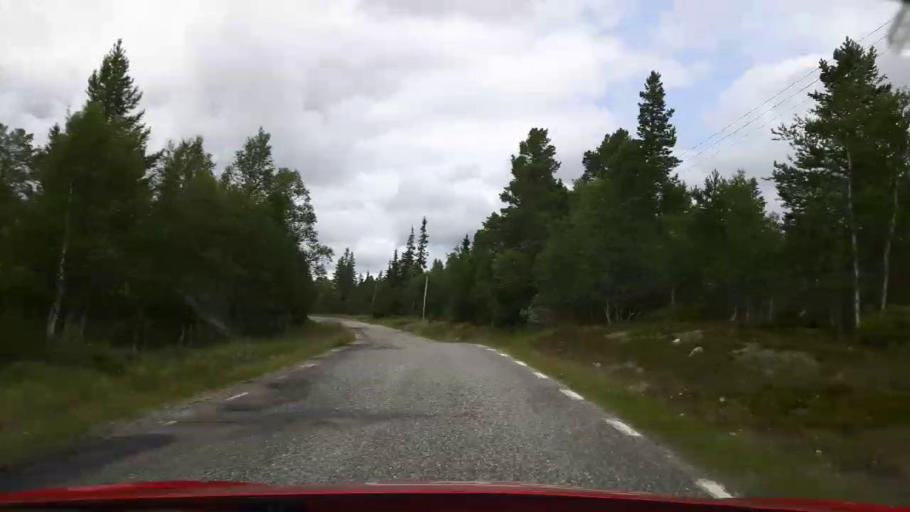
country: NO
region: Hedmark
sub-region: Engerdal
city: Engerdal
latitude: 62.3114
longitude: 12.8101
